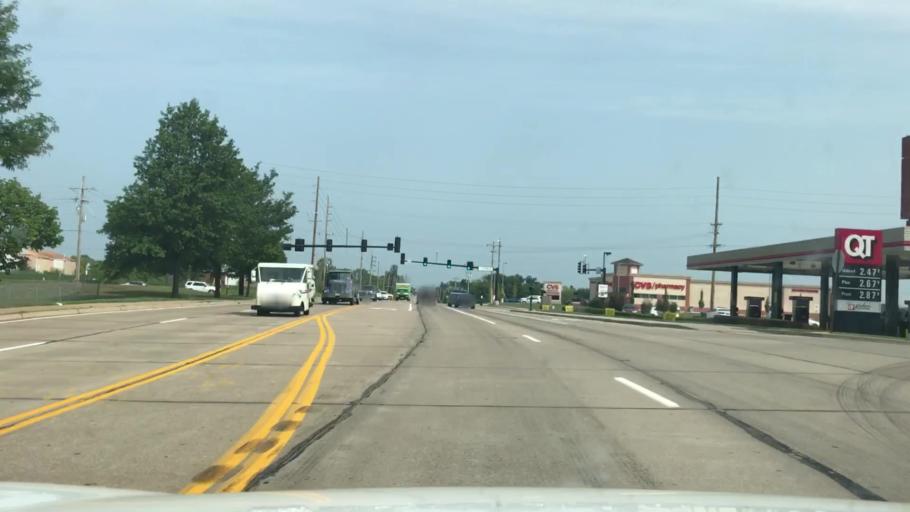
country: US
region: Missouri
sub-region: Saint Charles County
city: Dardenne Prairie
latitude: 38.7722
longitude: -90.7375
